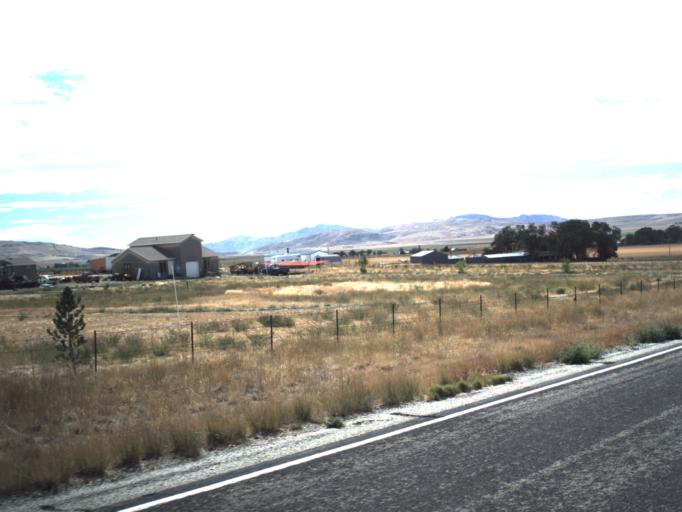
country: US
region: Utah
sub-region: Box Elder County
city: Garland
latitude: 41.7877
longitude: -112.4280
